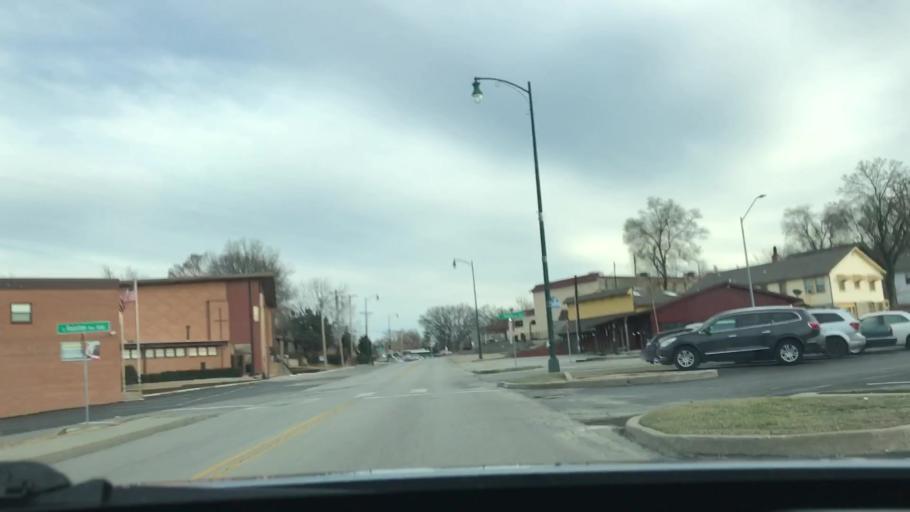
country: US
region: Missouri
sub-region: Jackson County
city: Sugar Creek
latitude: 39.0891
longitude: -94.4532
